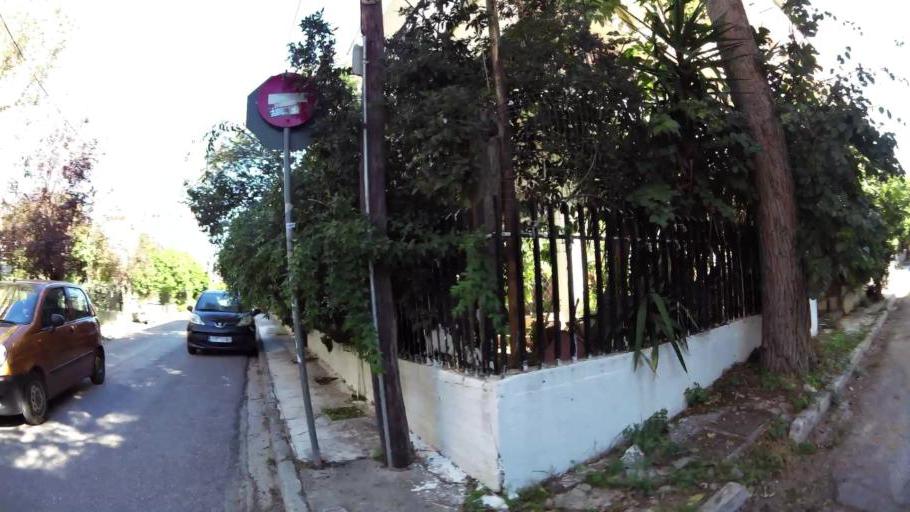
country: GR
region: Attica
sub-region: Nomarchia Athinas
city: Khalandrion
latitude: 38.0322
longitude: 23.8120
